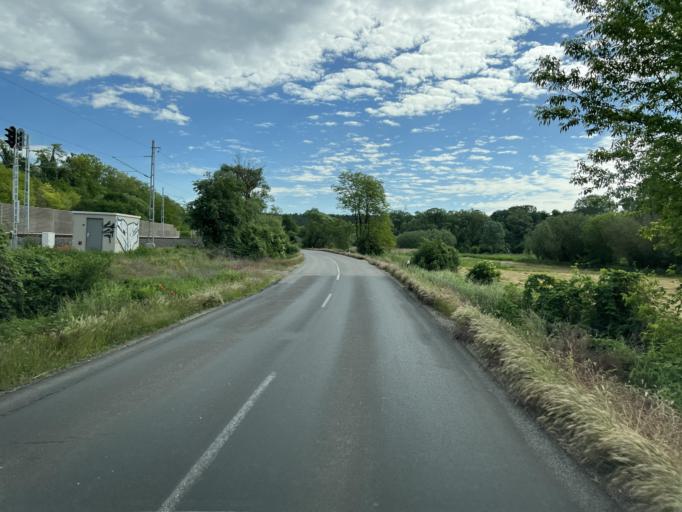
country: HU
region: Pest
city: Pecel
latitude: 47.4948
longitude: 19.3676
